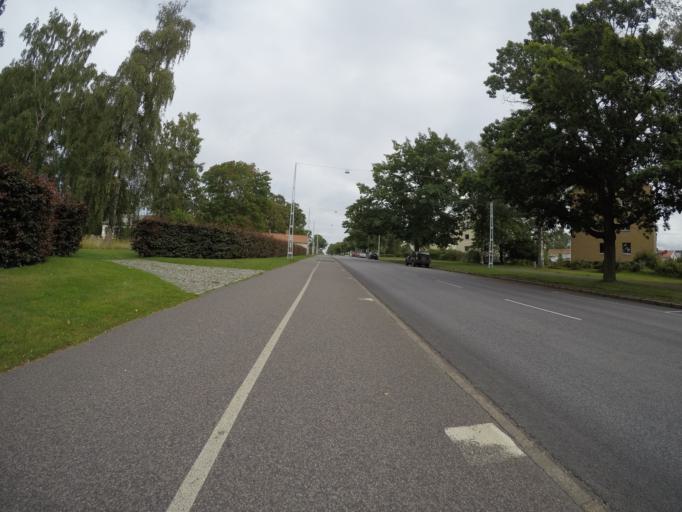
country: SE
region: Joenkoeping
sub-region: Jonkopings Kommun
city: Jonkoping
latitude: 57.7824
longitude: 14.2124
